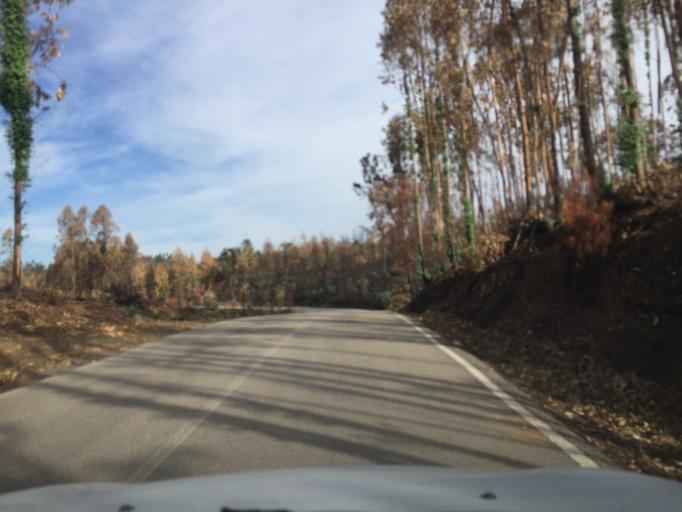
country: PT
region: Aveiro
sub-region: Mealhada
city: Mealhada
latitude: 40.3928
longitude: -8.3918
